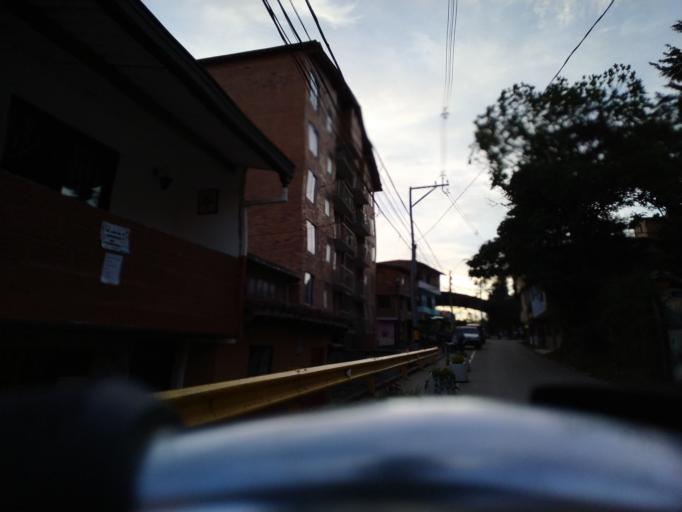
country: CO
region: Antioquia
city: Rionegro
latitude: 6.1596
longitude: -75.3776
